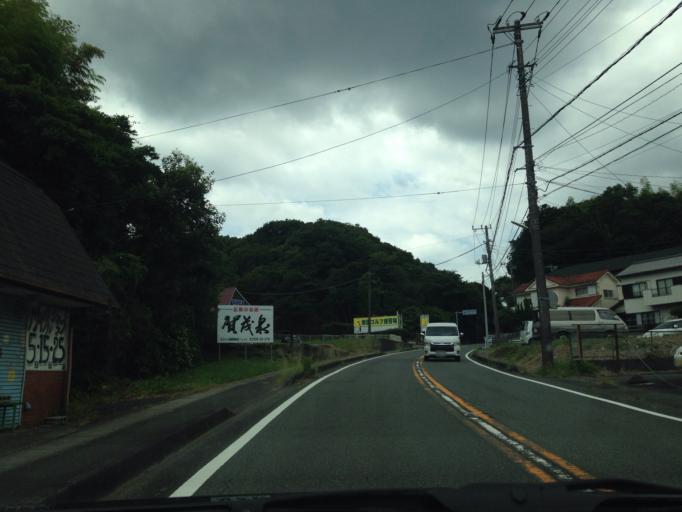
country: JP
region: Shizuoka
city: Shimoda
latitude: 34.6653
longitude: 138.9017
